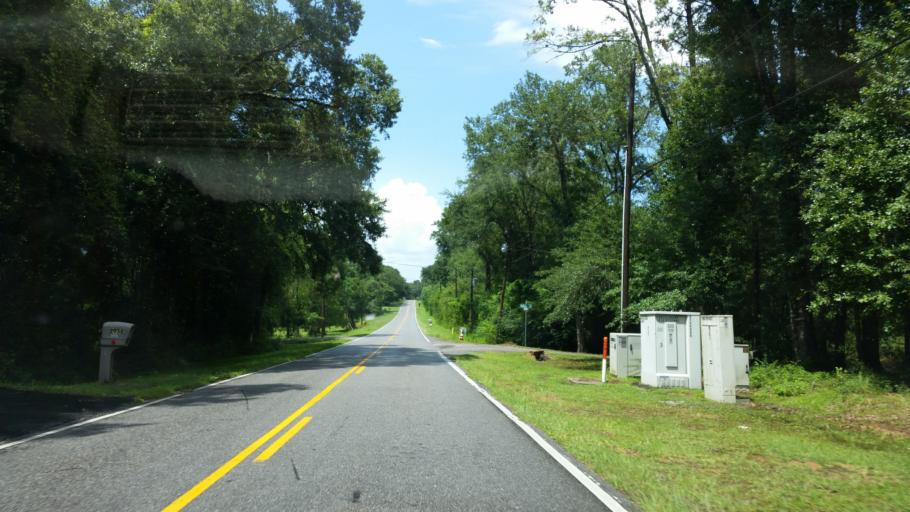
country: US
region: Florida
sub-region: Escambia County
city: Gonzalez
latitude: 30.5570
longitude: -87.2997
